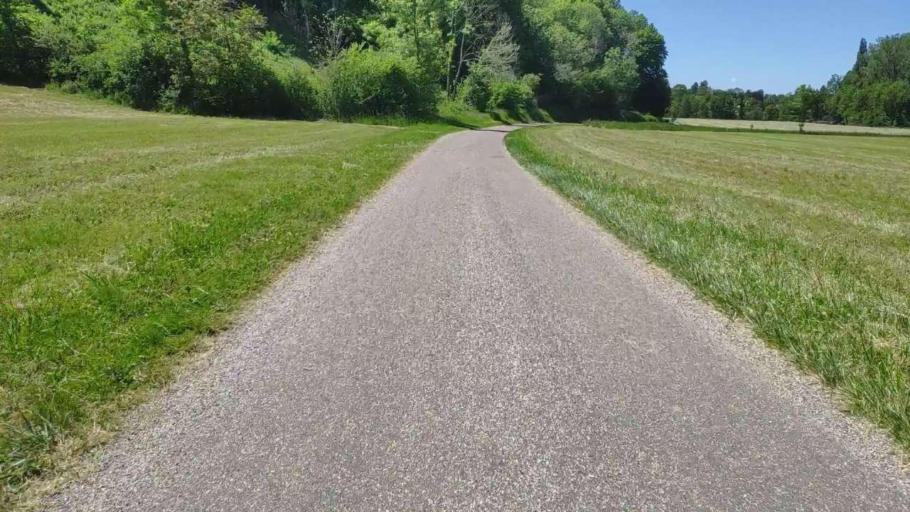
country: FR
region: Franche-Comte
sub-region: Departement du Jura
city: Perrigny
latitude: 46.7343
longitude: 5.6407
